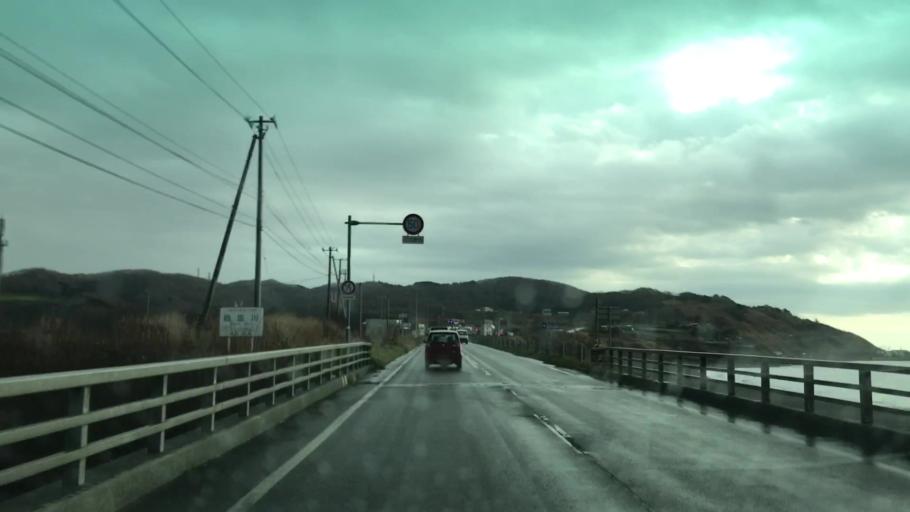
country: JP
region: Hokkaido
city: Shizunai-furukawacho
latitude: 42.1860
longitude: 142.7183
